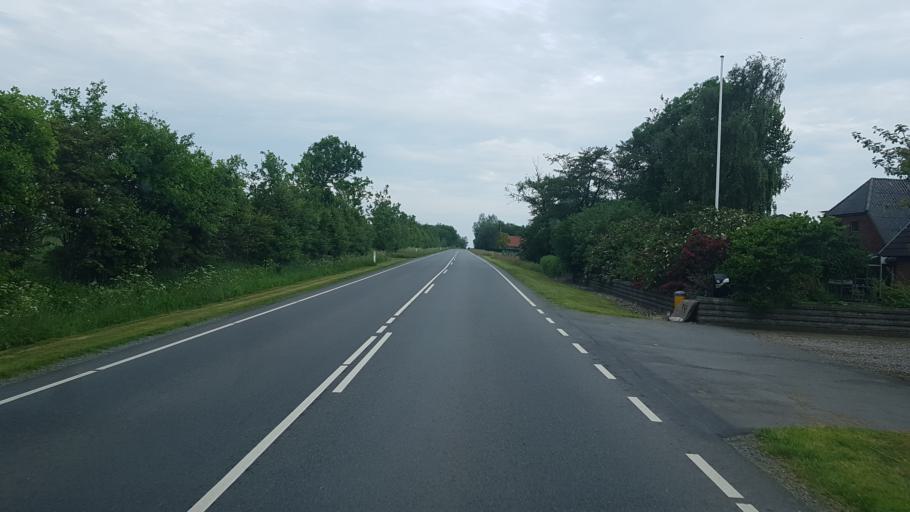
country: DK
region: South Denmark
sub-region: Vejen Kommune
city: Brorup
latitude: 55.4191
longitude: 9.0234
